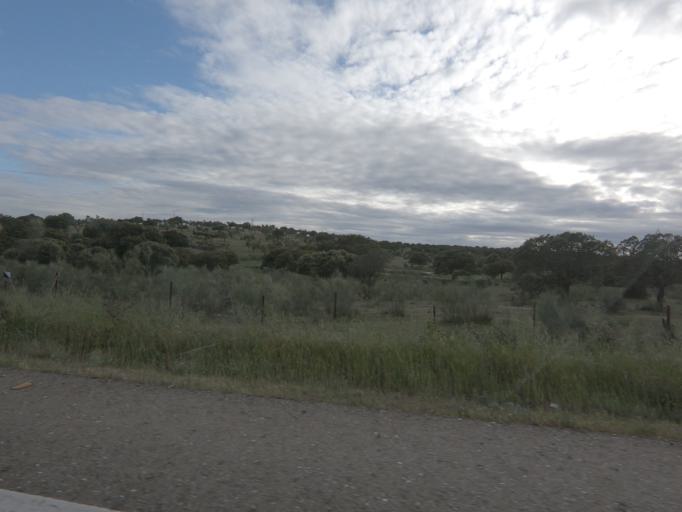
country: ES
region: Extremadura
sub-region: Provincia de Caceres
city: Torrejoncillo
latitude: 39.9096
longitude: -6.4804
